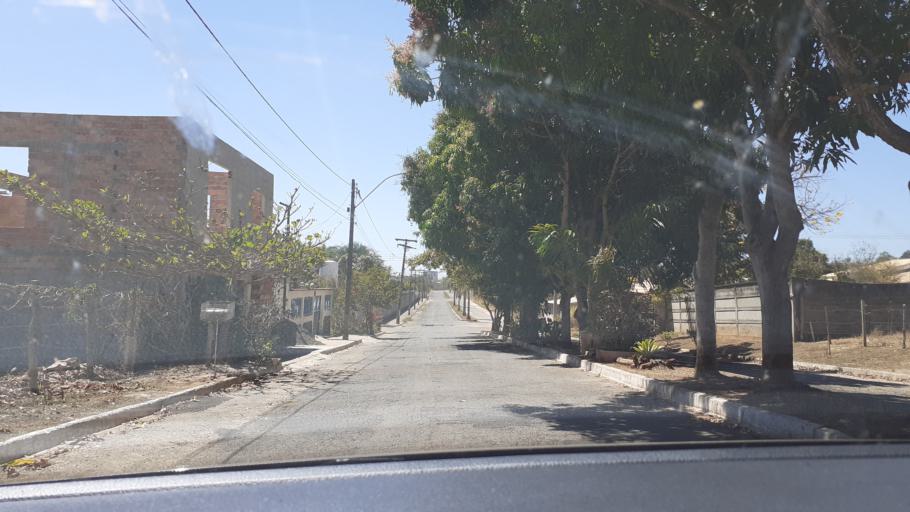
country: BR
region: Goias
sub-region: Caldas Novas
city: Caldas Novas
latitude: -17.7399
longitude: -48.6533
